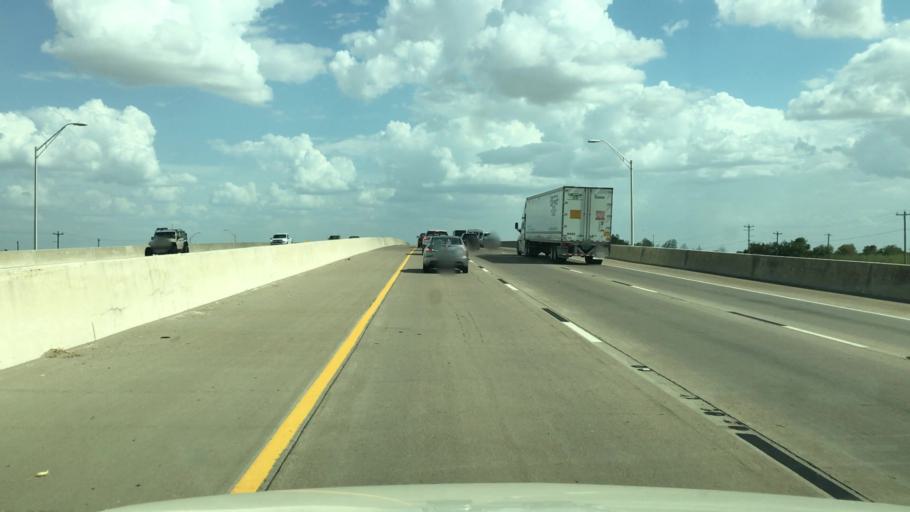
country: US
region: Texas
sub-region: Hill County
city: Hillsboro
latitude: 31.9409
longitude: -97.1086
